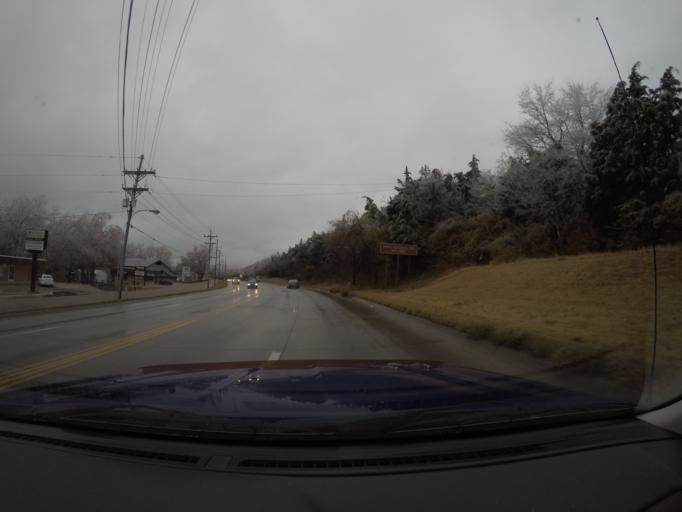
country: US
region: Kansas
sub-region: Riley County
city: Manhattan
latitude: 39.1744
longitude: -96.5881
